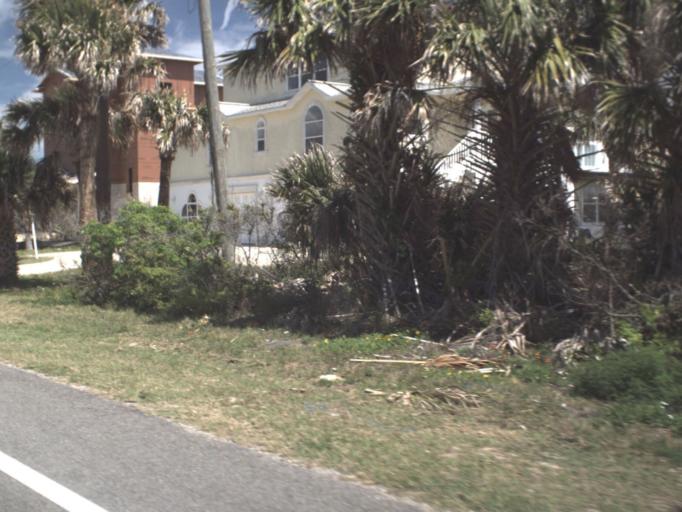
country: US
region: Florida
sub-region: Flagler County
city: Flagler Beach
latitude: 29.5180
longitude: -81.1461
